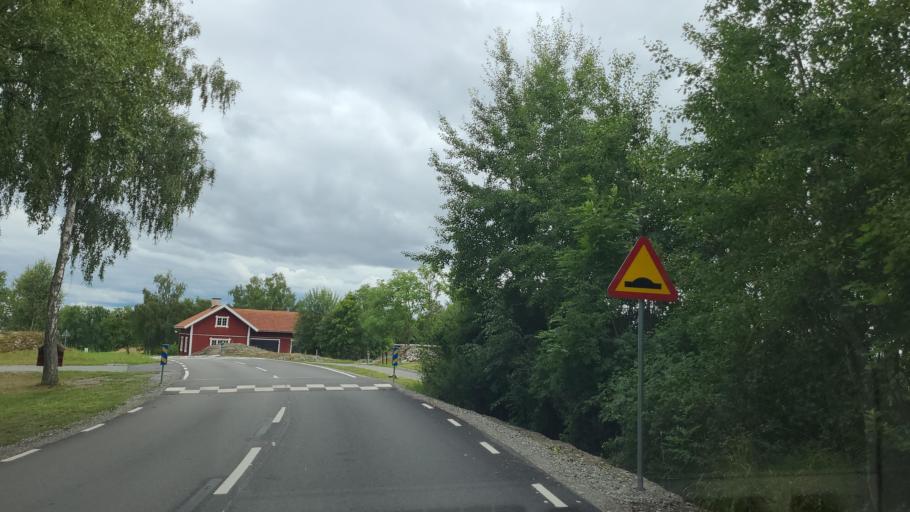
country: SE
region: Stockholm
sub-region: Upplands-Bro Kommun
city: Bro
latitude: 59.5021
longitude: 17.6256
